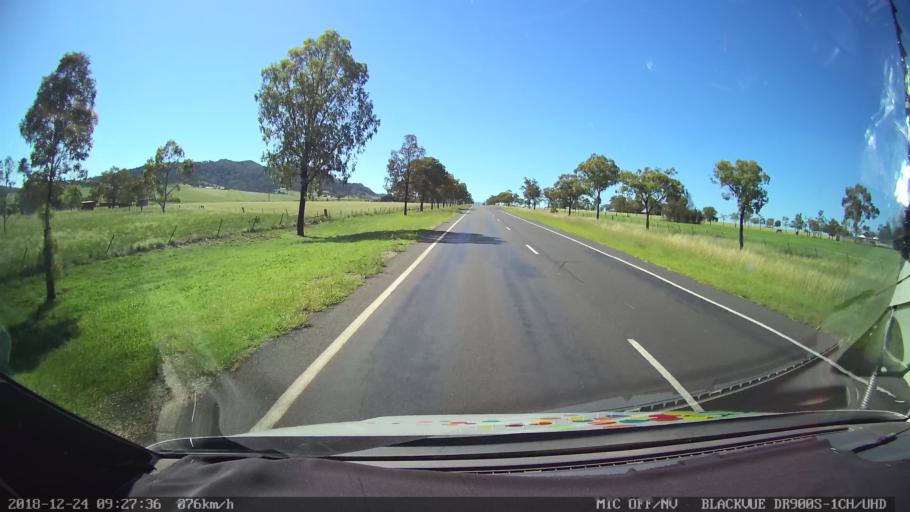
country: AU
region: New South Wales
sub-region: Liverpool Plains
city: Quirindi
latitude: -31.5296
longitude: 150.6823
